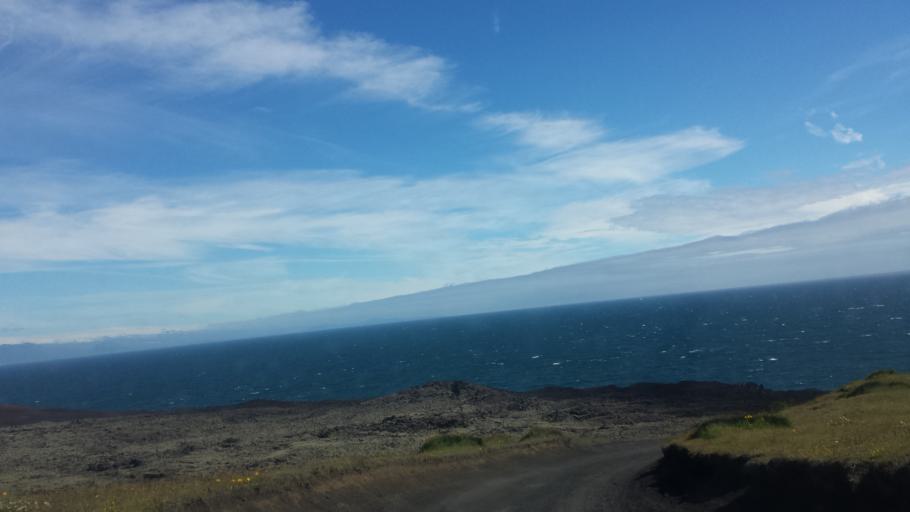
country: IS
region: South
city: Vestmannaeyjar
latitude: 63.4290
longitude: -20.2501
